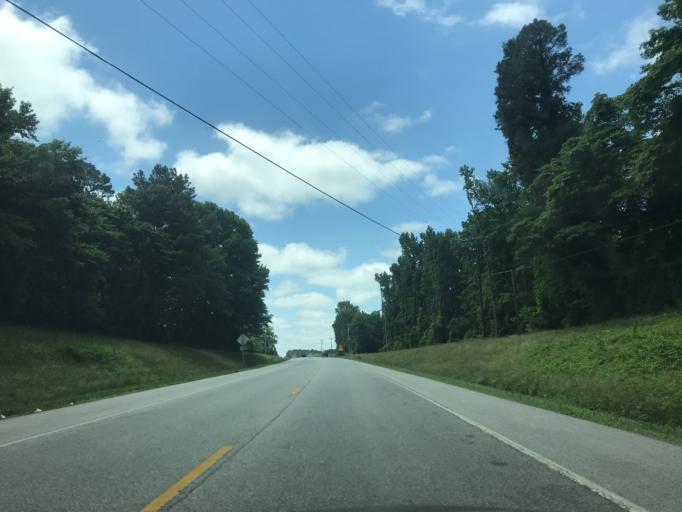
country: US
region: Maryland
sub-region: Caroline County
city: Federalsburg
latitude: 38.7128
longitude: -75.7886
